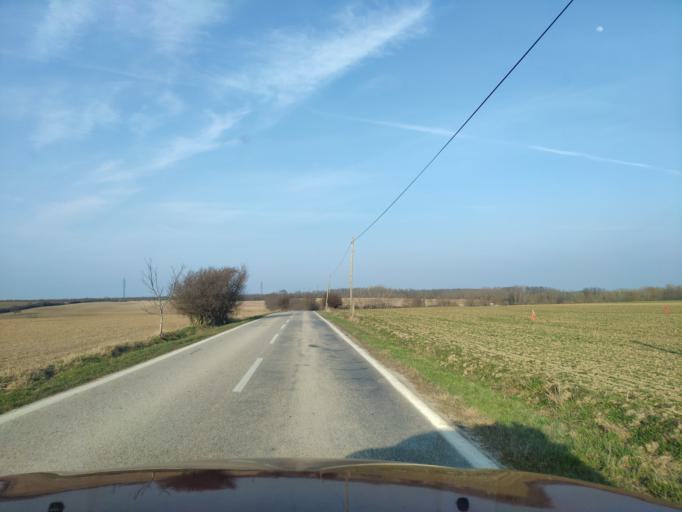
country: SK
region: Bratislavsky
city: Modra
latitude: 48.3077
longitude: 17.3527
